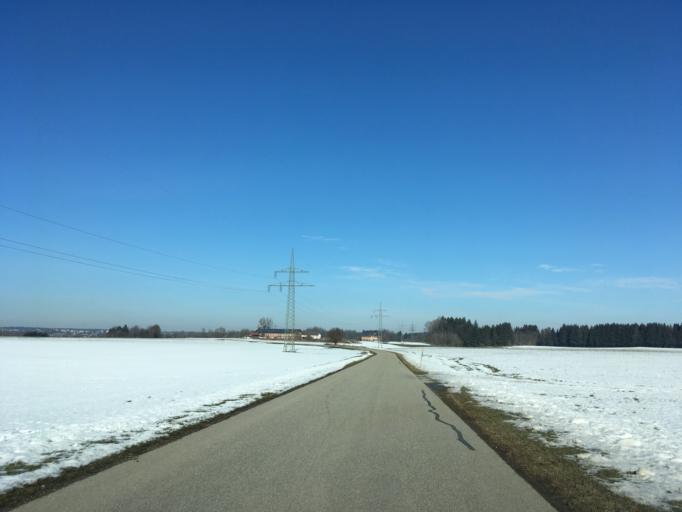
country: DE
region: Bavaria
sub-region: Upper Bavaria
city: Vogtareuth
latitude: 47.9548
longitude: 12.1716
